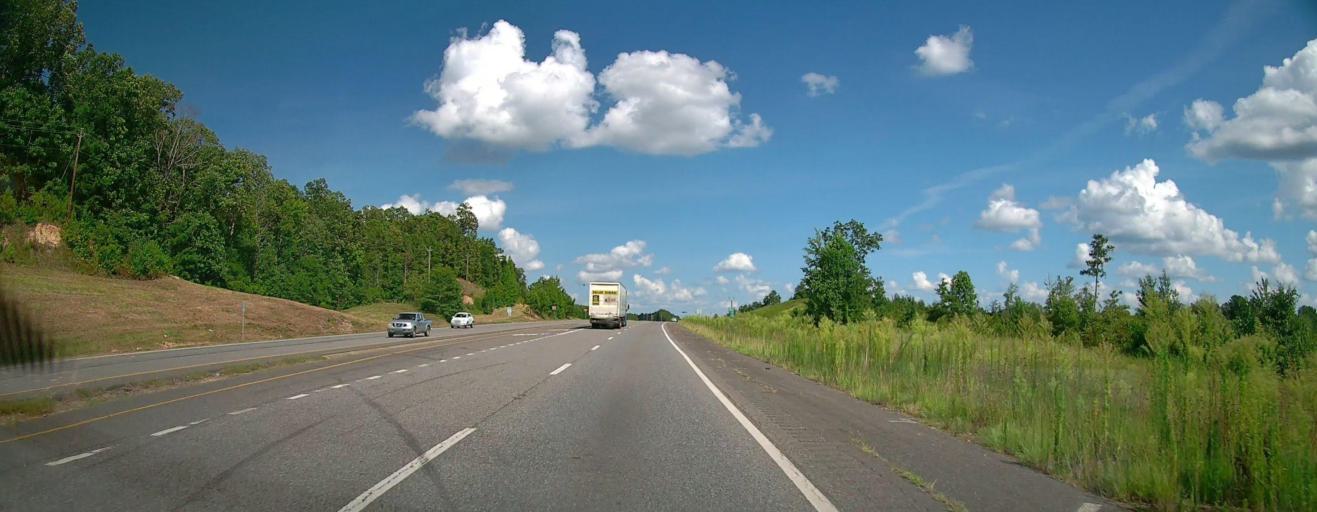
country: US
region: Alabama
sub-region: Tuscaloosa County
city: Northport
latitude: 33.2648
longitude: -87.7122
